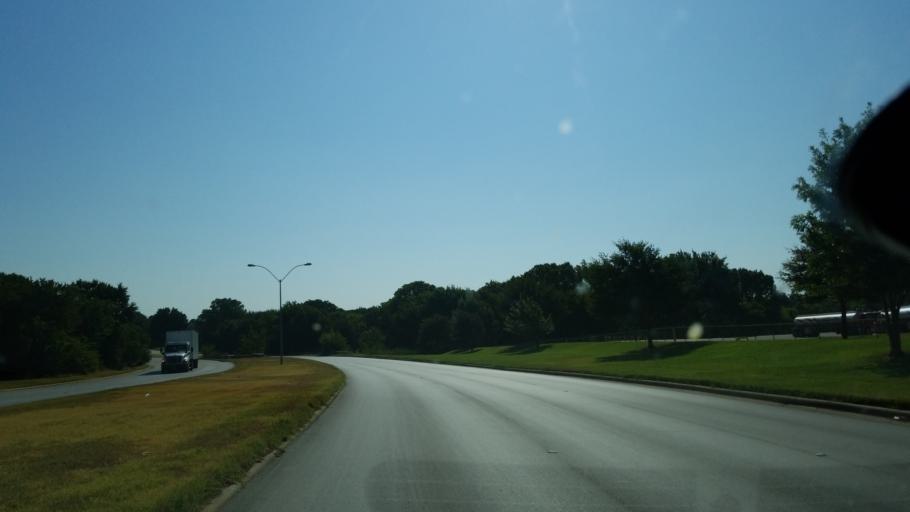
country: US
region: Texas
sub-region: Tarrant County
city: Euless
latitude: 32.8166
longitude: -97.0941
